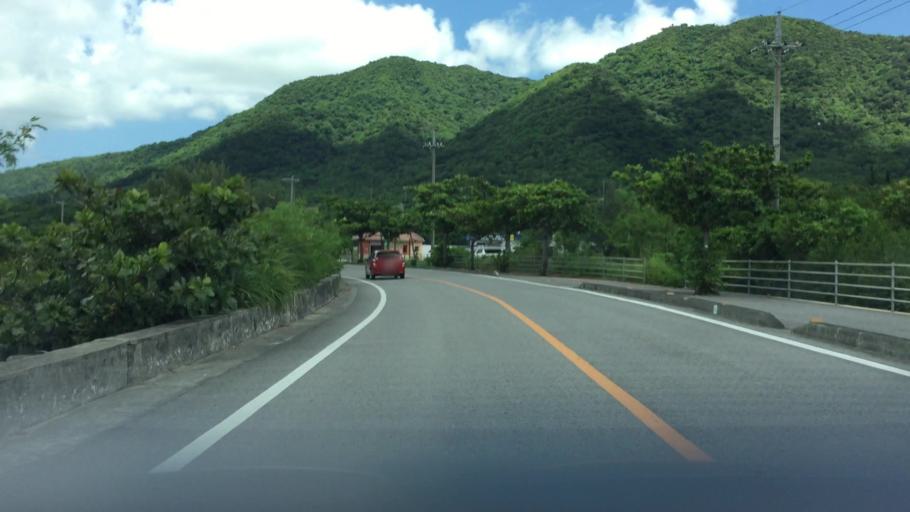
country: JP
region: Okinawa
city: Ishigaki
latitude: 24.4127
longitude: 124.1437
